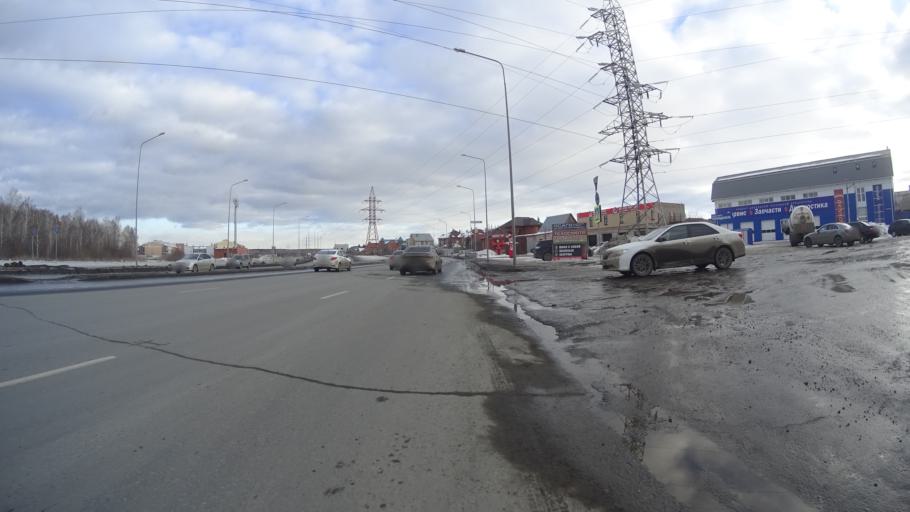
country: RU
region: Chelyabinsk
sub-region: Gorod Chelyabinsk
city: Chelyabinsk
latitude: 55.1573
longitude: 61.3063
